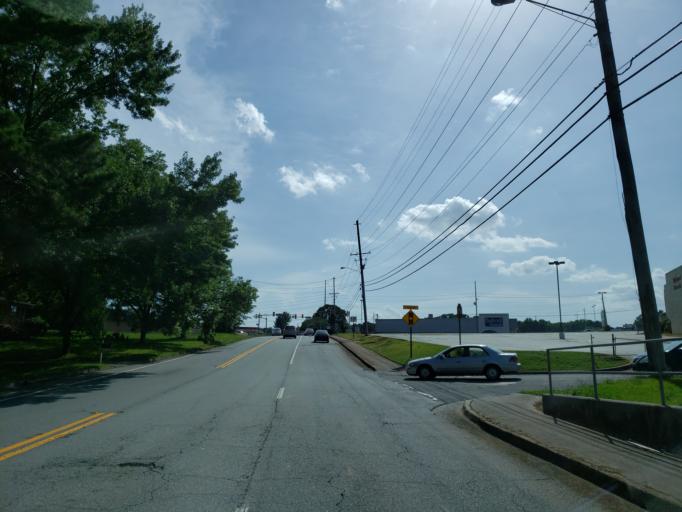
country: US
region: Georgia
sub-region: Cobb County
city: Mableton
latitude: 33.8626
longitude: -84.5928
